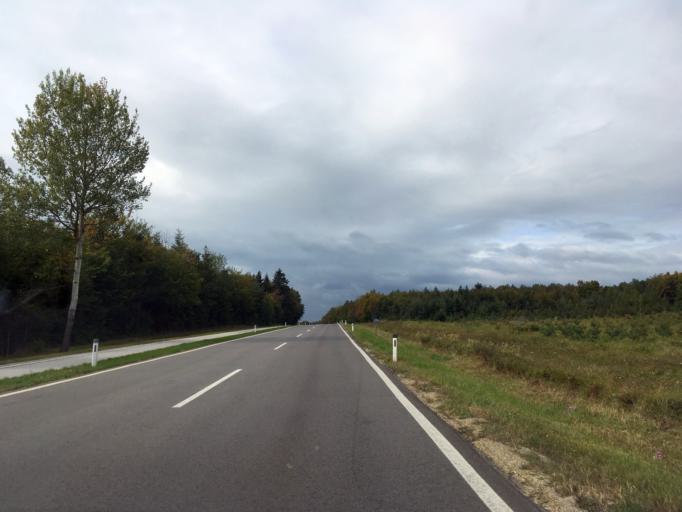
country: AT
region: Lower Austria
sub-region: Politischer Bezirk Modling
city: Gaaden
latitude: 48.0548
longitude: 16.1724
